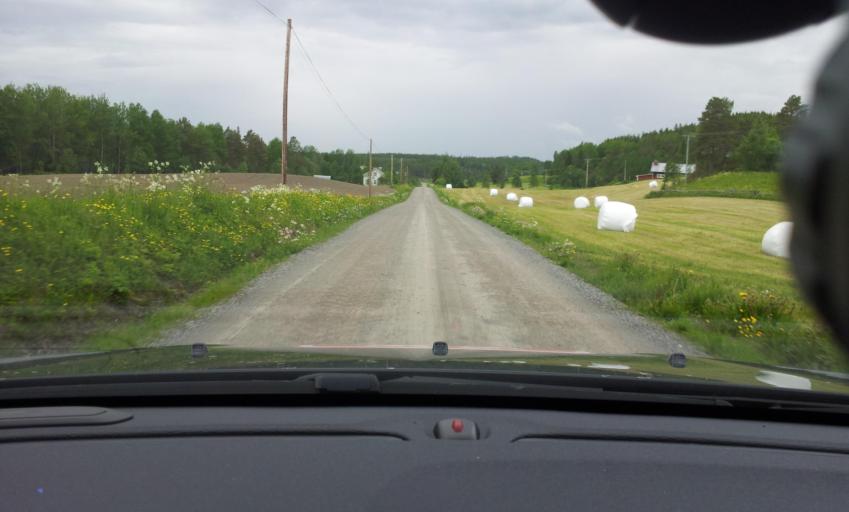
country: SE
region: Jaemtland
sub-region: OEstersunds Kommun
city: Brunflo
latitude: 62.9693
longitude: 14.6920
